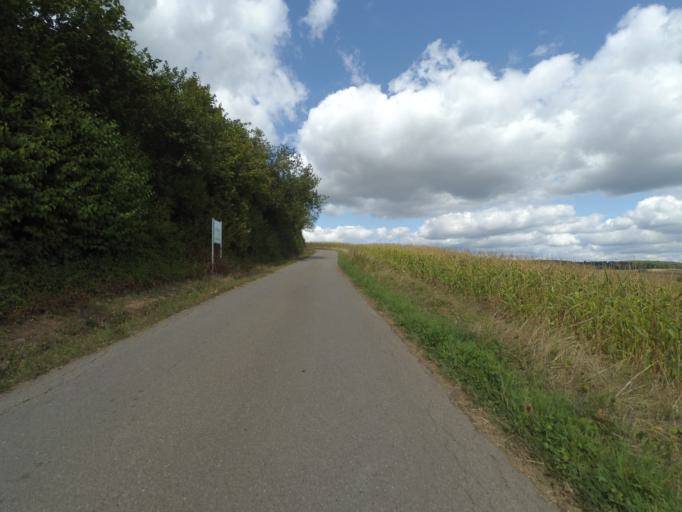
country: LU
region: Grevenmacher
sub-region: Canton de Grevenmacher
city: Betzdorf
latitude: 49.6848
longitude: 6.3389
